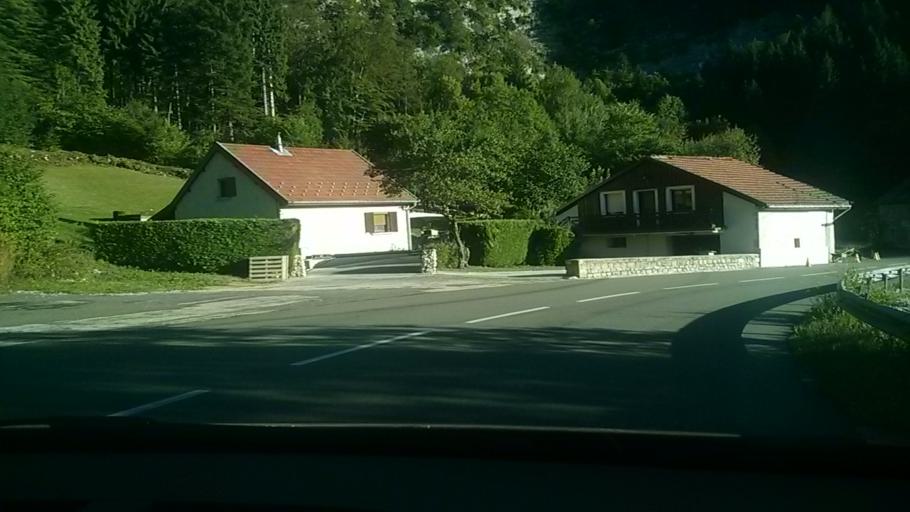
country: FR
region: Franche-Comte
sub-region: Departement du Jura
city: Saint-Claude
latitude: 46.3548
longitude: 5.9069
